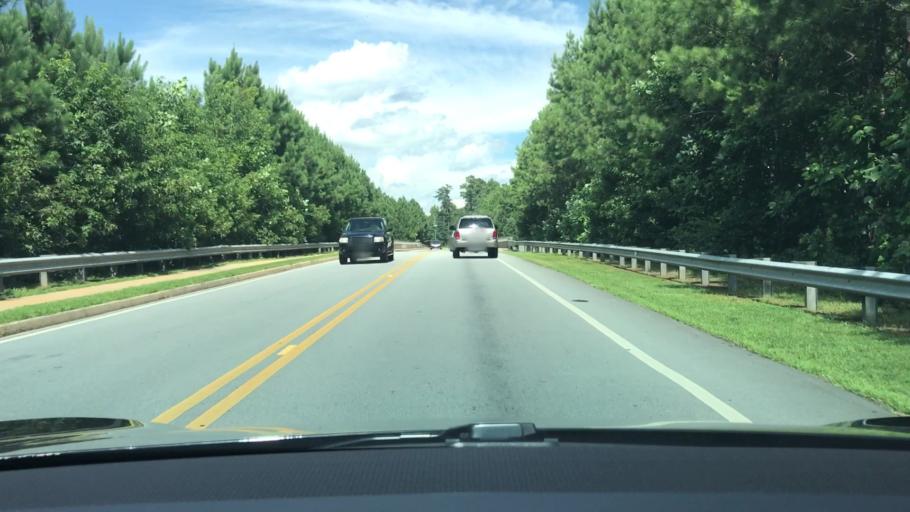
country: US
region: Georgia
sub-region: Gwinnett County
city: Sugar Hill
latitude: 34.0823
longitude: -84.0485
